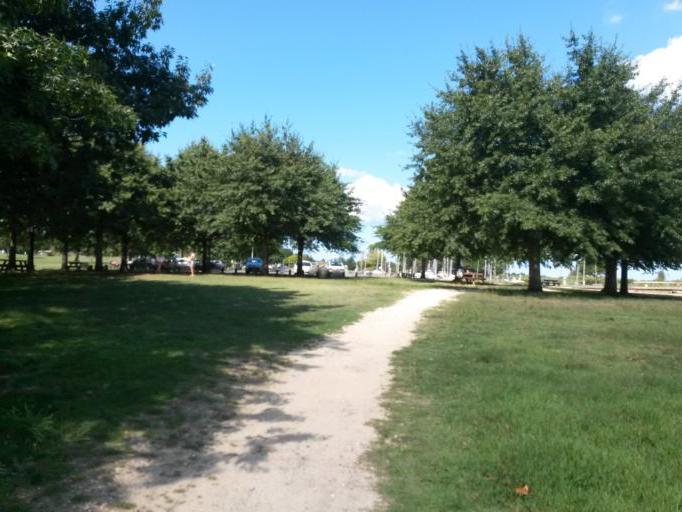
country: FR
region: Aquitaine
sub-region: Departement de la Gironde
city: Le Teich
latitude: 44.6395
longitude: -1.0157
